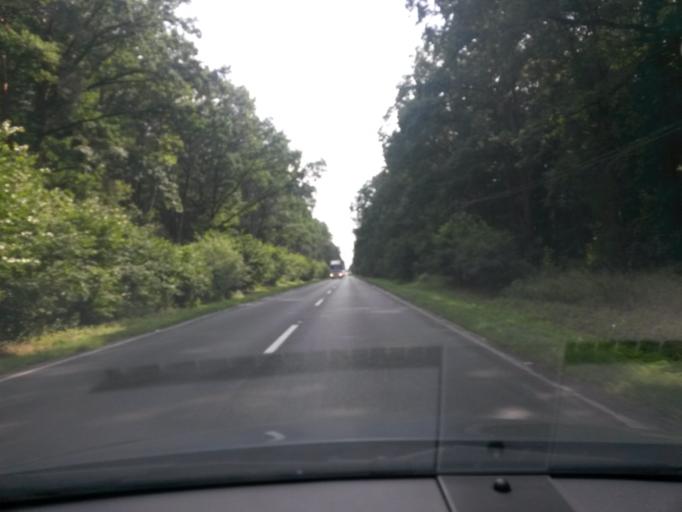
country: PL
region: Greater Poland Voivodeship
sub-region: Powiat poznanski
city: Kornik
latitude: 52.2121
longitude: 17.0703
